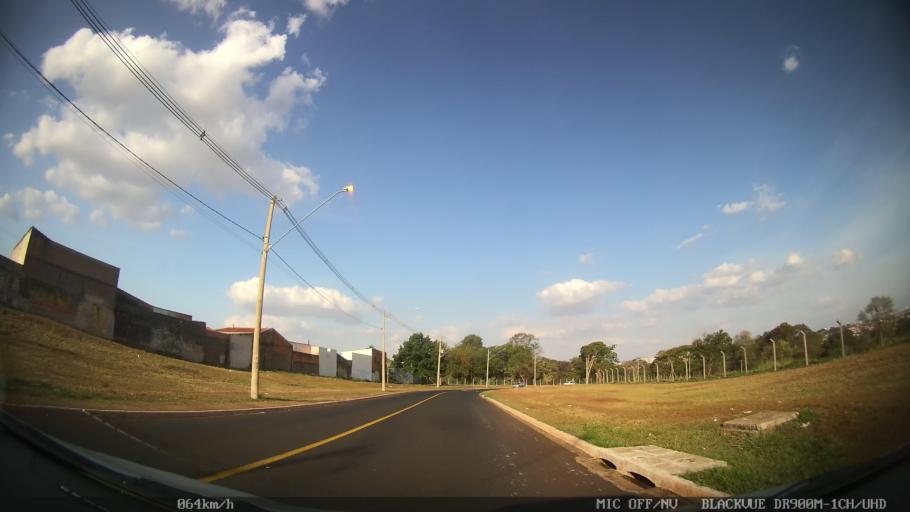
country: BR
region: Sao Paulo
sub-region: Ribeirao Preto
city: Ribeirao Preto
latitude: -21.1694
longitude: -47.8449
